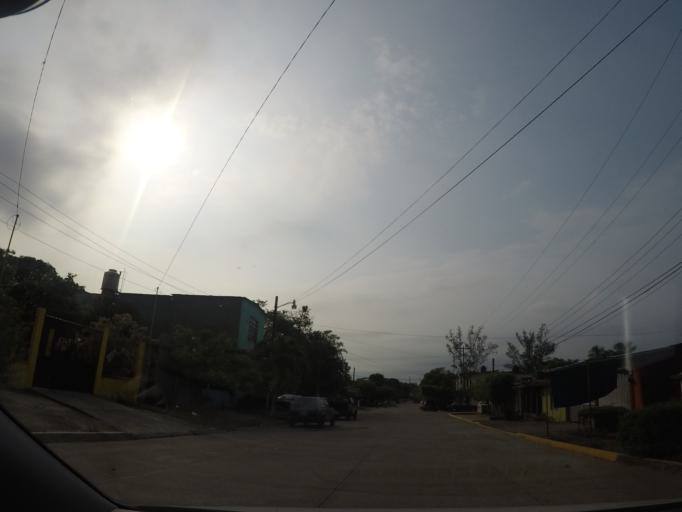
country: MX
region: Oaxaca
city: Colonia Rincon Viejo
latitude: 16.8843
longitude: -95.0425
